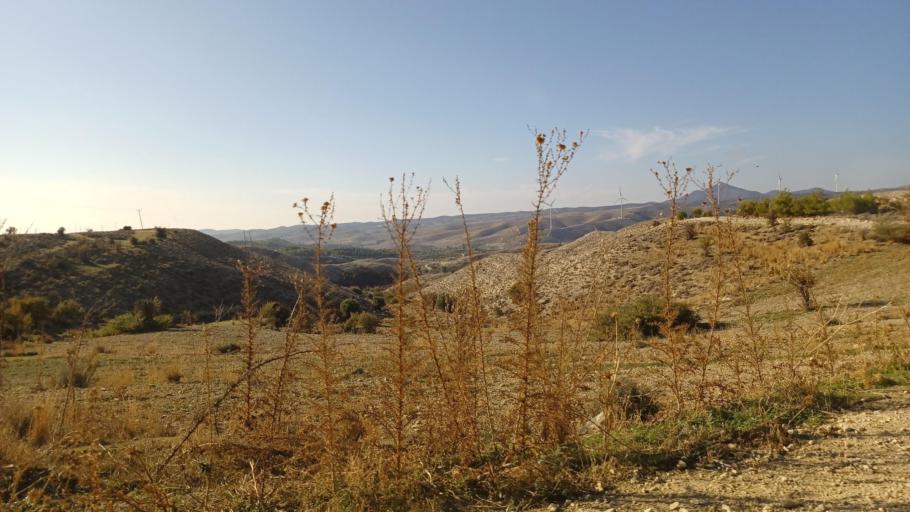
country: CY
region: Larnaka
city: Psevdas
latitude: 34.9504
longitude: 33.5118
